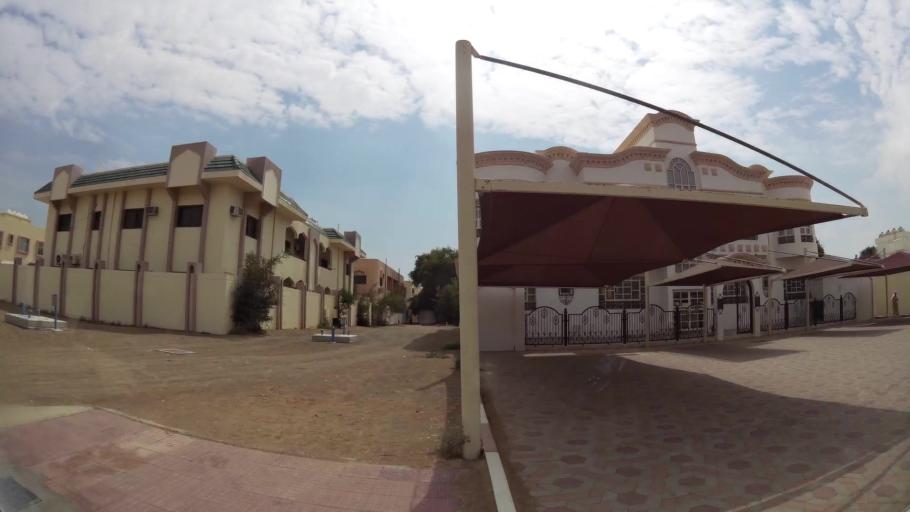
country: AE
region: Abu Dhabi
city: Al Ain
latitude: 24.2145
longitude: 55.7879
